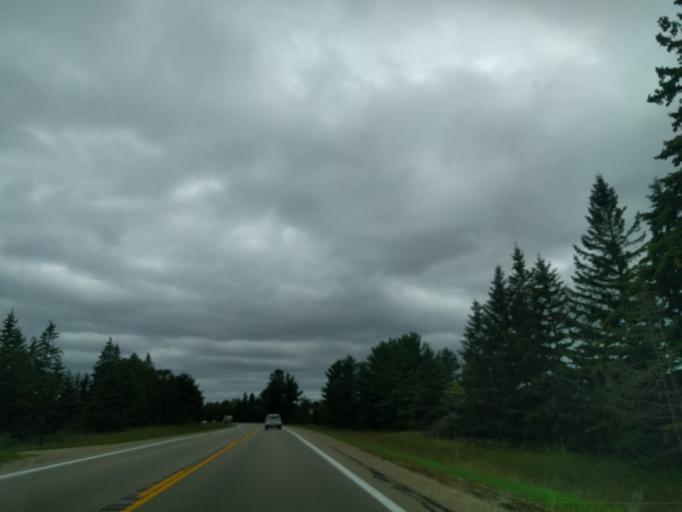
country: US
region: Michigan
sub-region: Delta County
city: Escanaba
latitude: 45.4844
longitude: -87.3045
